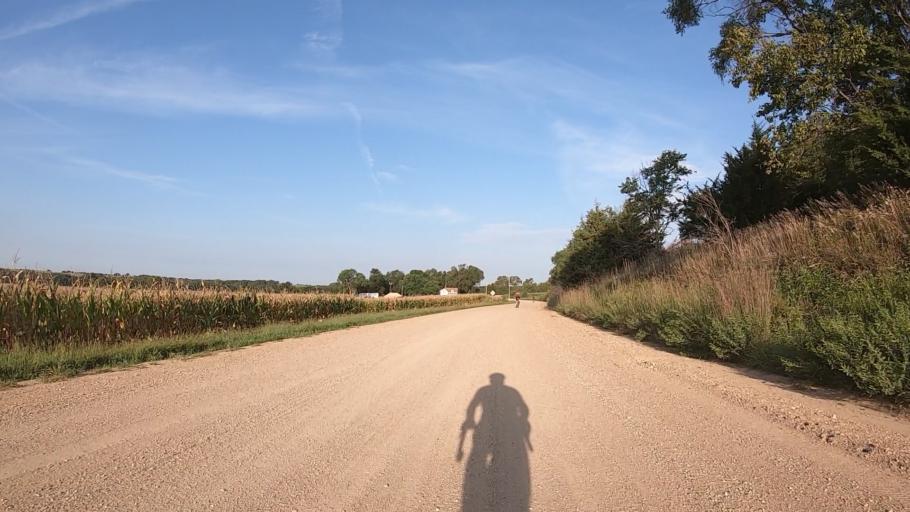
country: US
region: Kansas
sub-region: Marshall County
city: Blue Rapids
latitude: 39.7260
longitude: -96.7893
